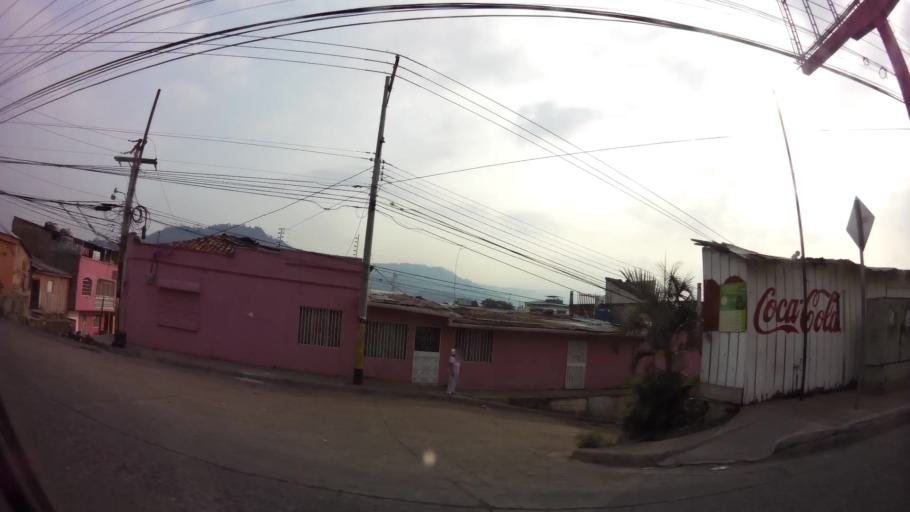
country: HN
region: Francisco Morazan
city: Tegucigalpa
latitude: 14.0970
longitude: -87.1993
